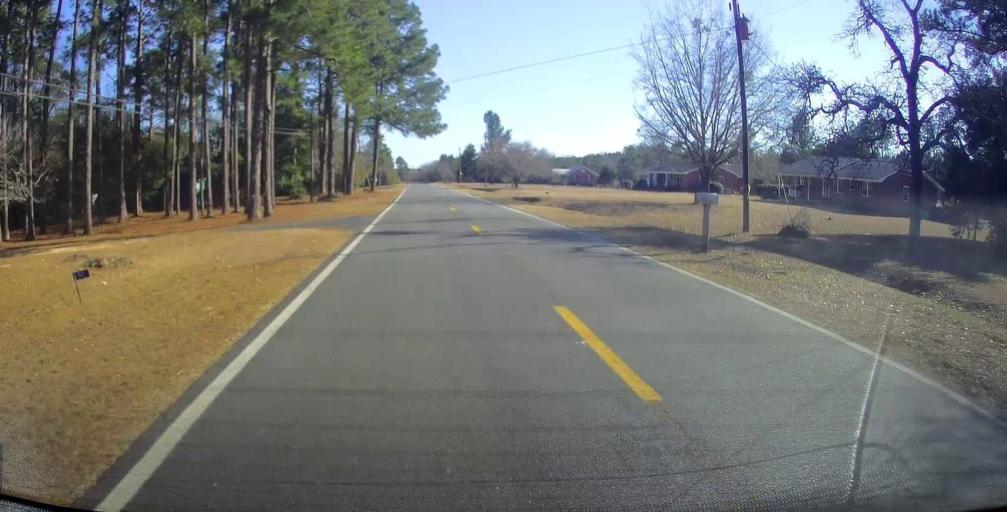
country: US
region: Georgia
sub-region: Taylor County
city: Butler
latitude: 32.5495
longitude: -84.2291
